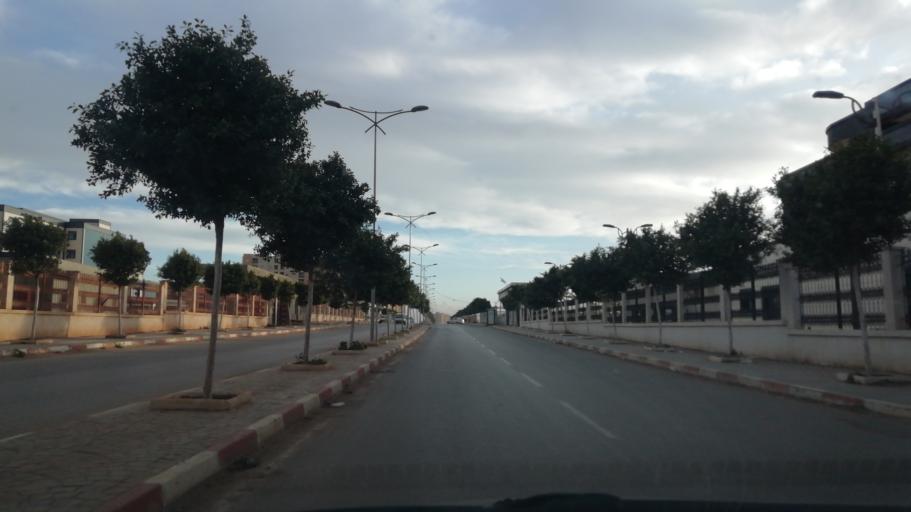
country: DZ
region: Oran
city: Bir el Djir
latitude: 35.6953
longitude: -0.5854
